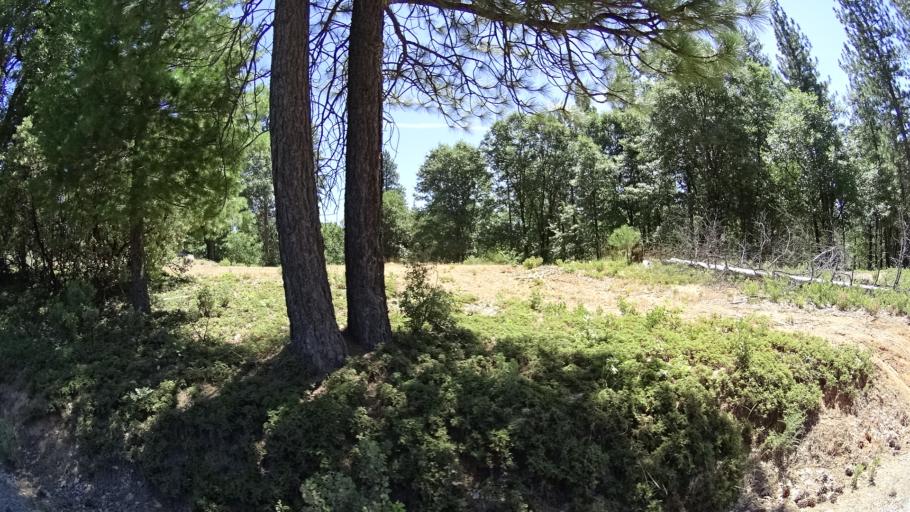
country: US
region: California
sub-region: Amador County
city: Pioneer
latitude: 38.4194
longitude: -120.5019
